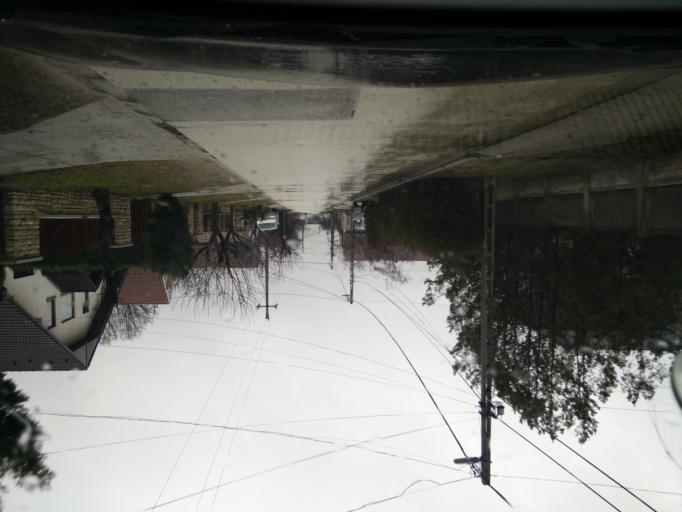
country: HU
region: Pest
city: Pilisszentivan
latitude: 47.6130
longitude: 18.8981
